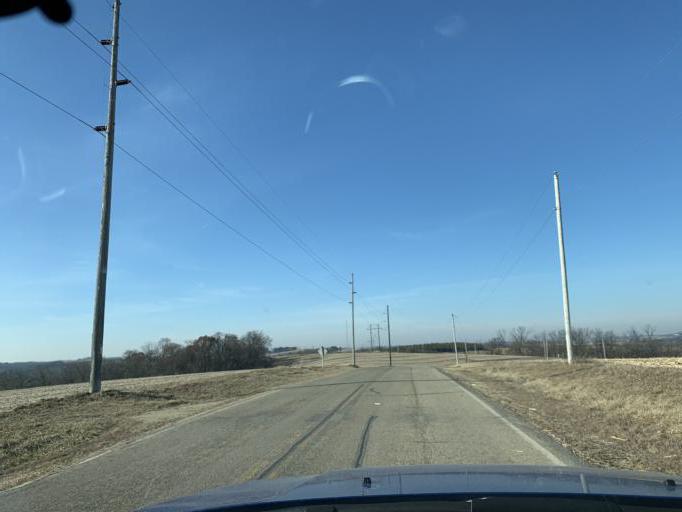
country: US
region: Wisconsin
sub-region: Iowa County
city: Barneveld
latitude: 42.8585
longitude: -89.9385
